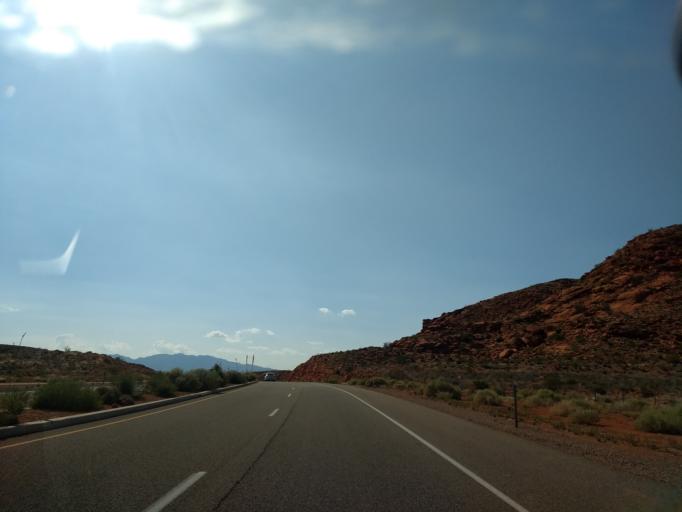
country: US
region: Utah
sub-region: Washington County
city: Saint George
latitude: 37.1334
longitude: -113.5873
